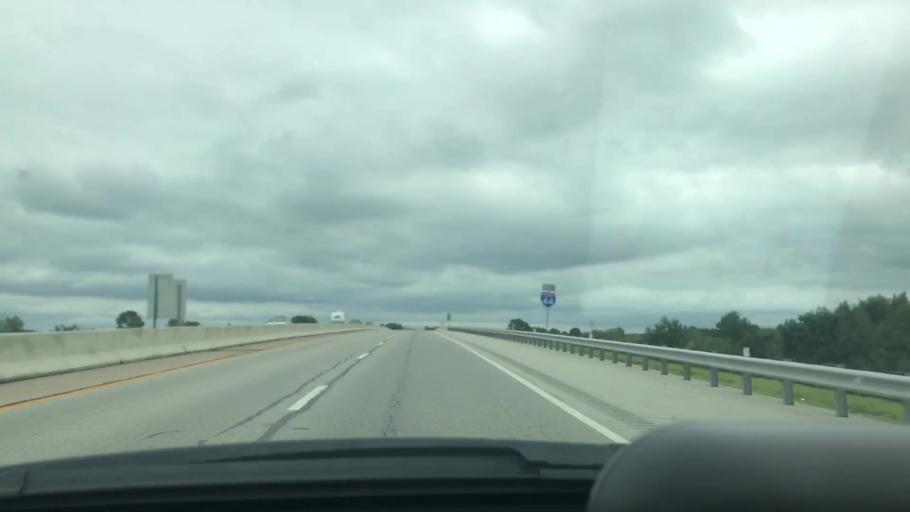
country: US
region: Oklahoma
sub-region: Ottawa County
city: Afton
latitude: 36.7244
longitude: -94.9292
